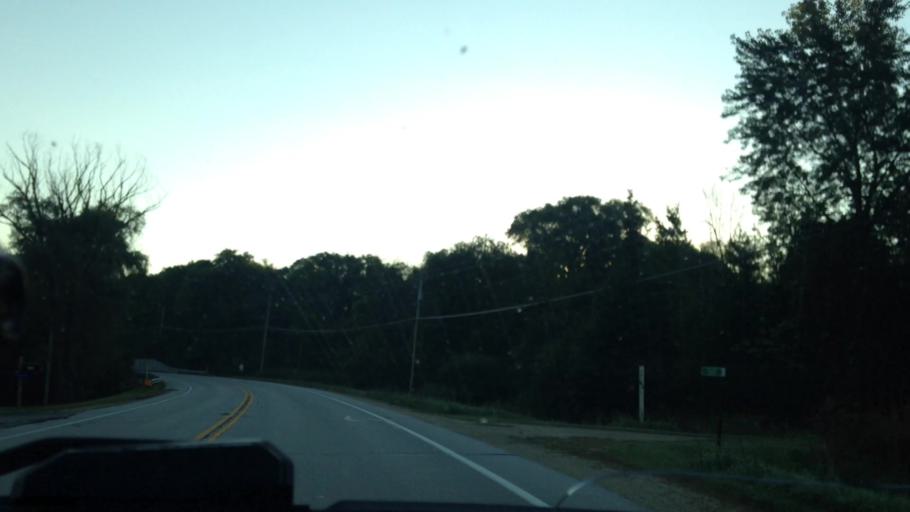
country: US
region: Wisconsin
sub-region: Washington County
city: Newburg
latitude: 43.4232
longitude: -88.0640
